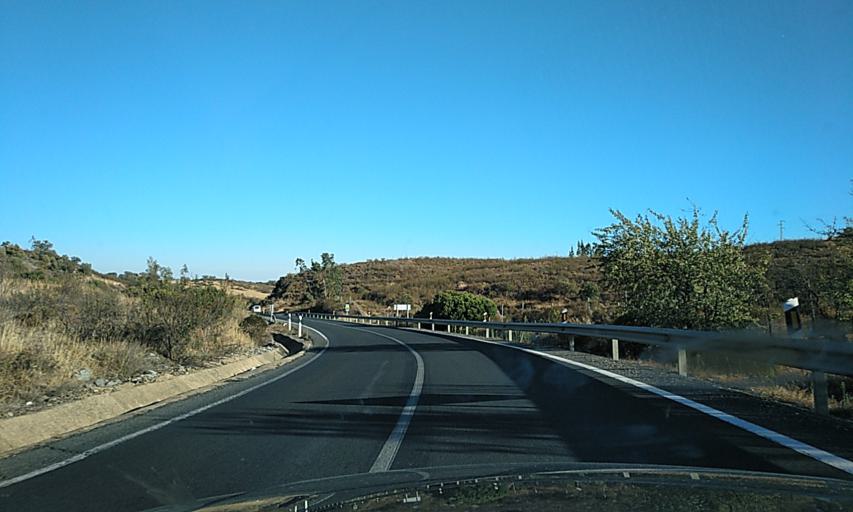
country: ES
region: Andalusia
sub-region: Provincia de Huelva
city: San Bartolome de la Torre
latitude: 37.4786
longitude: -7.1278
